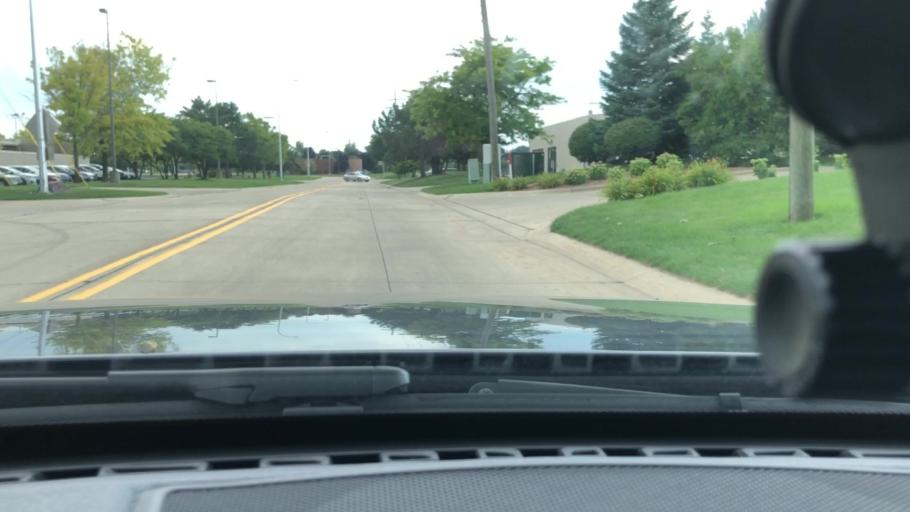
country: US
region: Michigan
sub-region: Wayne County
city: Livonia
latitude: 42.3719
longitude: -83.3404
